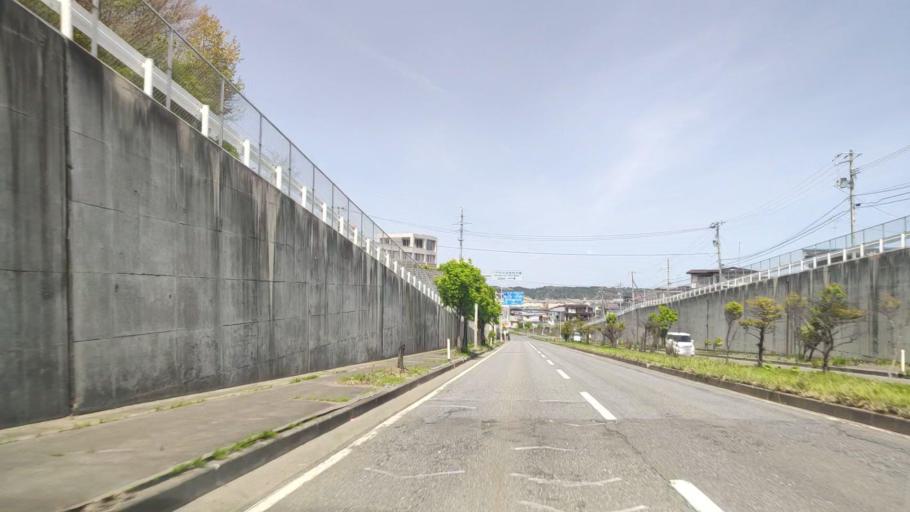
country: JP
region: Aomori
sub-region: Hachinohe Shi
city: Uchimaru
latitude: 40.4988
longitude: 141.4567
